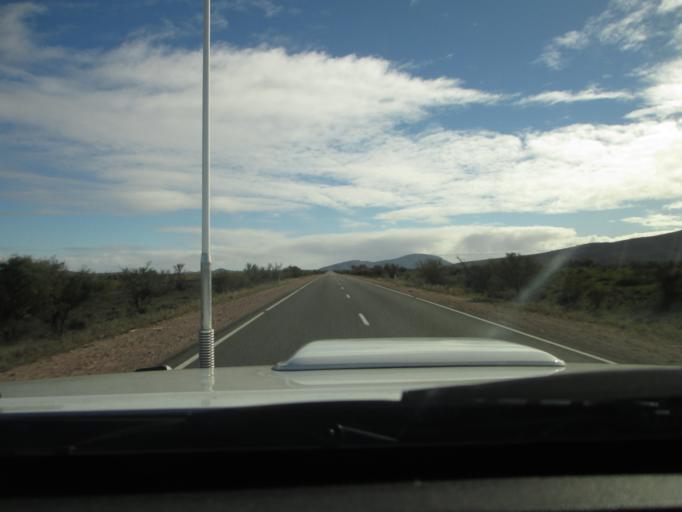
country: AU
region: South Australia
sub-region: Flinders Ranges
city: Quorn
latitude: -31.8613
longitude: 138.4030
